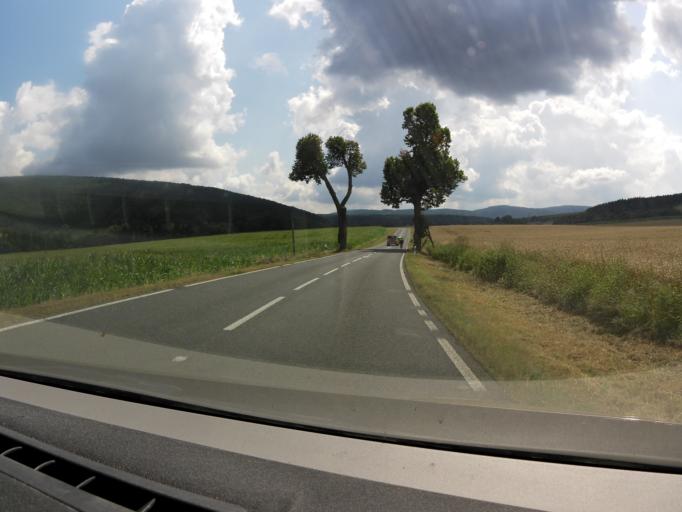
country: DE
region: Thuringia
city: Neusiss
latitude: 50.7385
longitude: 10.8888
